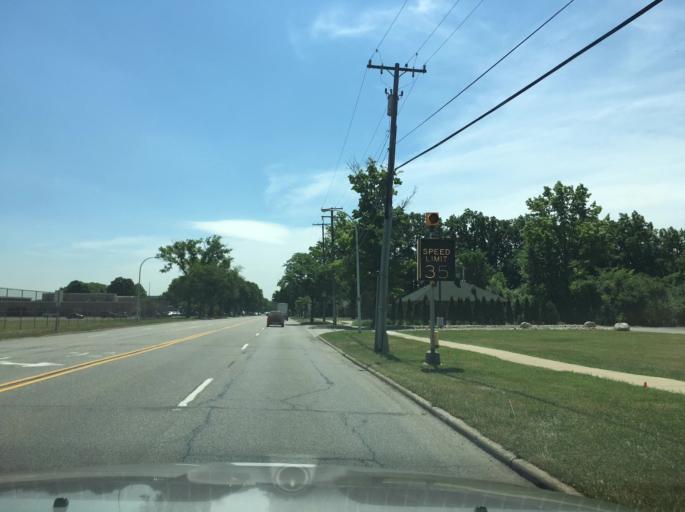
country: US
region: Michigan
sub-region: Wayne County
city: Allen Park
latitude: 42.2947
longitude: -83.2191
